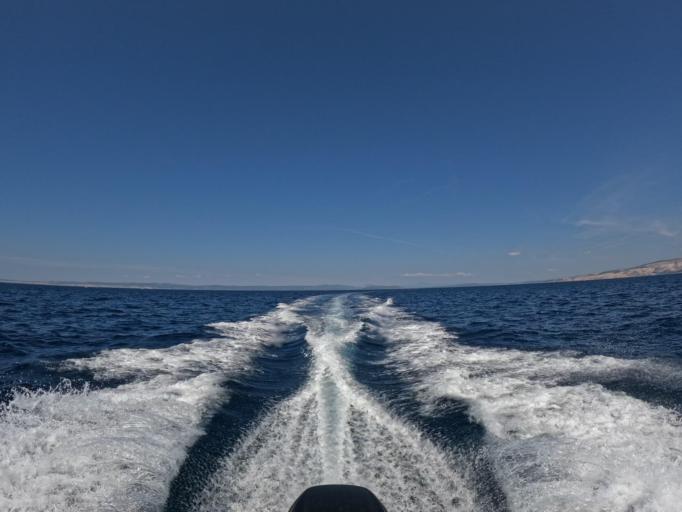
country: HR
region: Primorsko-Goranska
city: Lopar
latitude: 44.8740
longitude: 14.6647
